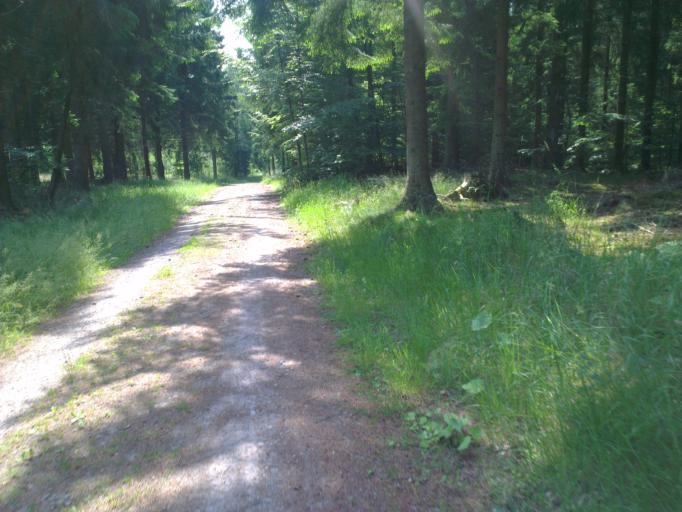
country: DK
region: Capital Region
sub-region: Allerod Kommune
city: Blovstrod
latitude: 55.9028
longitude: 12.3711
